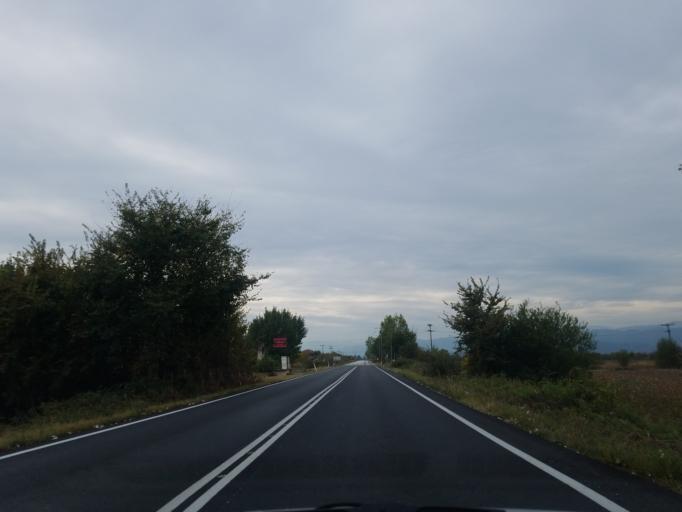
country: GR
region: Thessaly
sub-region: Nomos Kardhitsas
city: Agnantero
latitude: 39.4955
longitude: 21.8385
